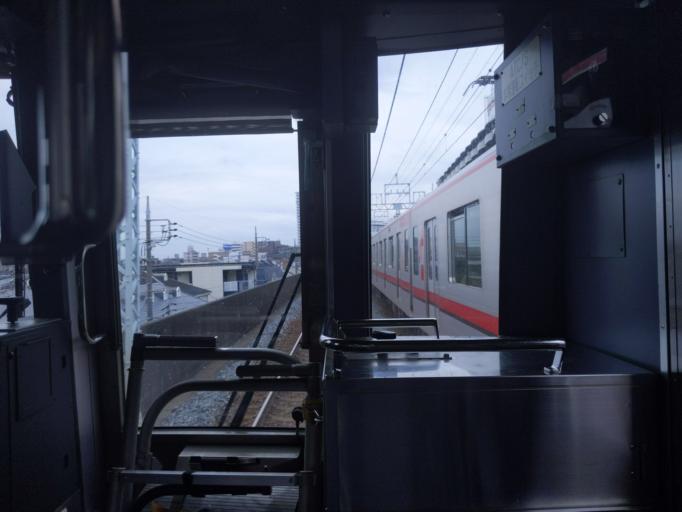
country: JP
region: Saitama
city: Soka
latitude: 35.8191
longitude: 139.8026
